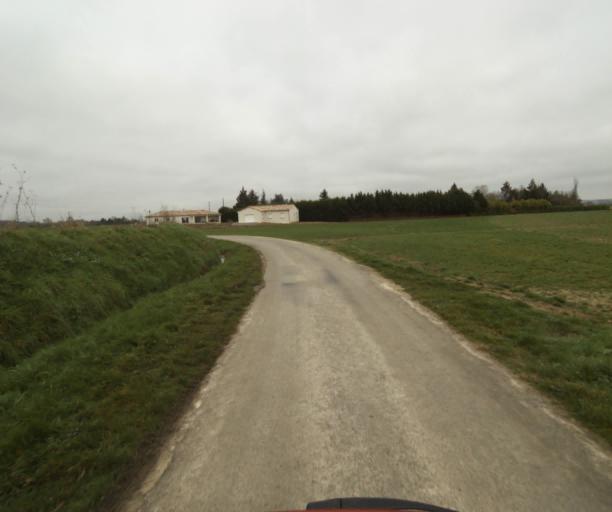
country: FR
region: Midi-Pyrenees
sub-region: Departement de l'Ariege
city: Saverdun
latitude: 43.2584
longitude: 1.5301
